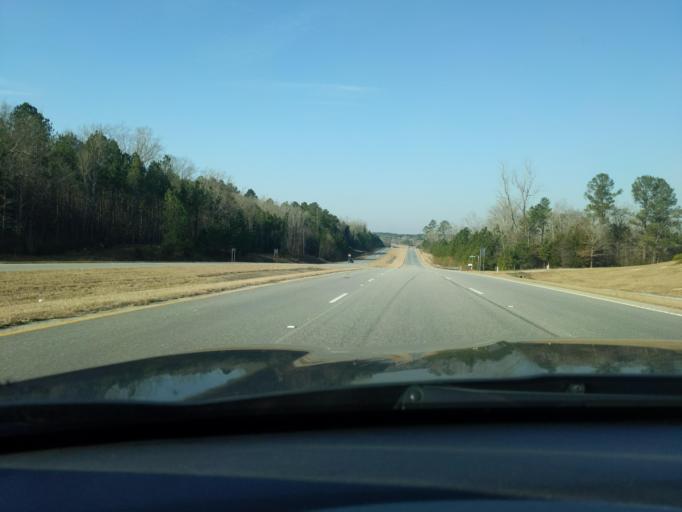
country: US
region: South Carolina
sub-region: Abbeville County
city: Calhoun Falls
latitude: 34.1112
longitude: -82.4982
